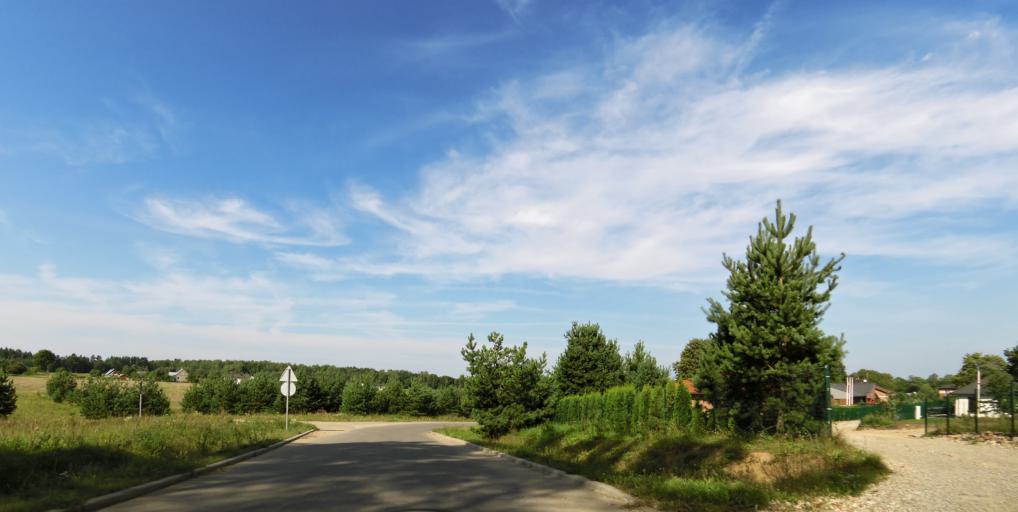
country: LT
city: Grigiskes
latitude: 54.7250
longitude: 25.0768
